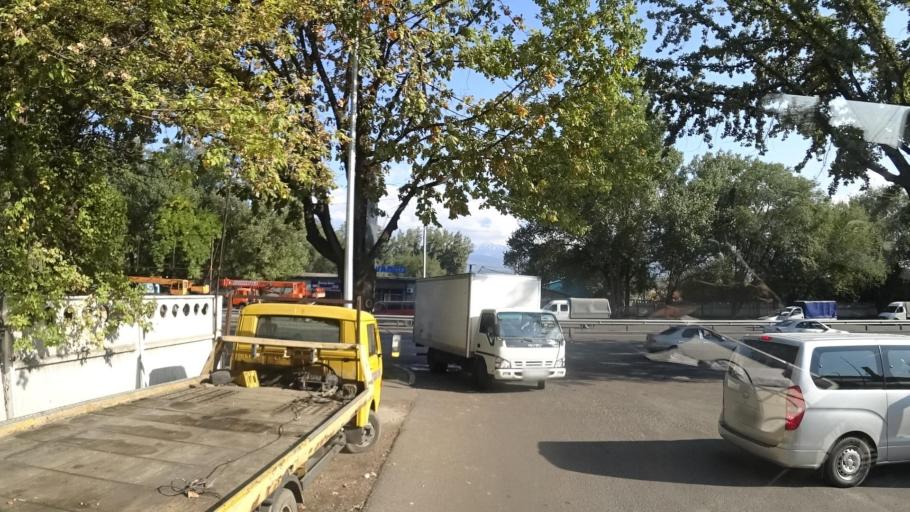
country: KZ
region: Almaty Qalasy
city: Almaty
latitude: 43.2881
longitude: 76.9233
